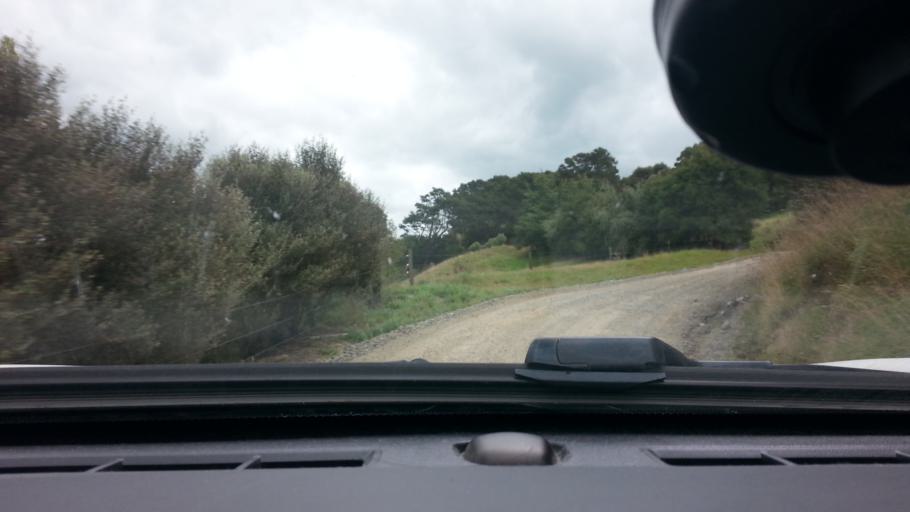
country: NZ
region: Wellington
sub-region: Masterton District
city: Masterton
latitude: -41.1500
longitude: 175.4814
